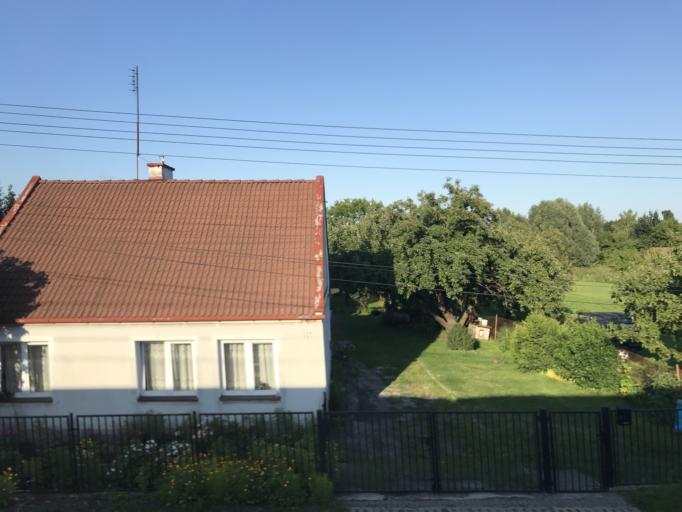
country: PL
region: Pomeranian Voivodeship
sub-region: Powiat gdanski
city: Pruszcz Gdanski
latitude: 54.3049
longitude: 18.6350
